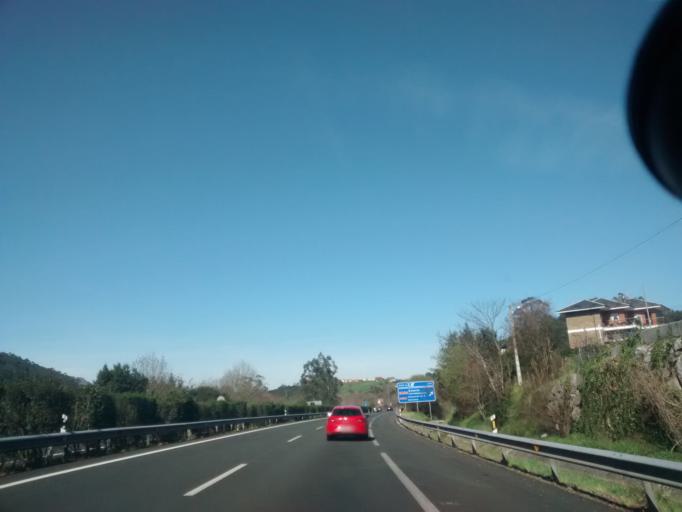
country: ES
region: Cantabria
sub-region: Provincia de Cantabria
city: Entrambasaguas
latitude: 43.3910
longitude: -3.6944
